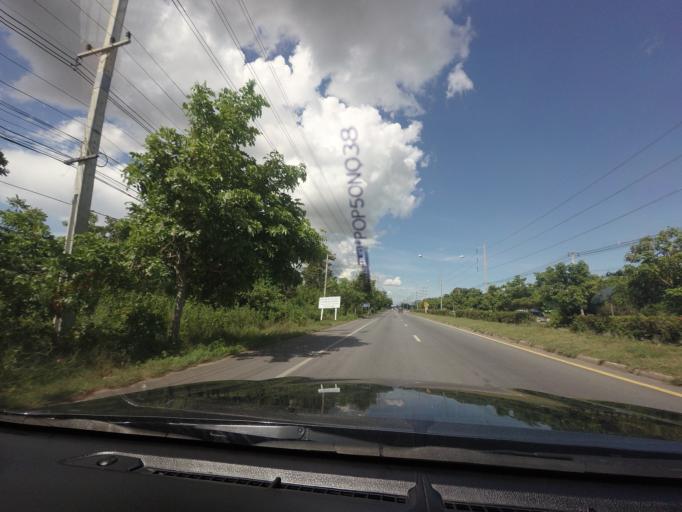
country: TH
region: Kanchanaburi
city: Phanom Thuan
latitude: 14.1179
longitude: 99.6805
